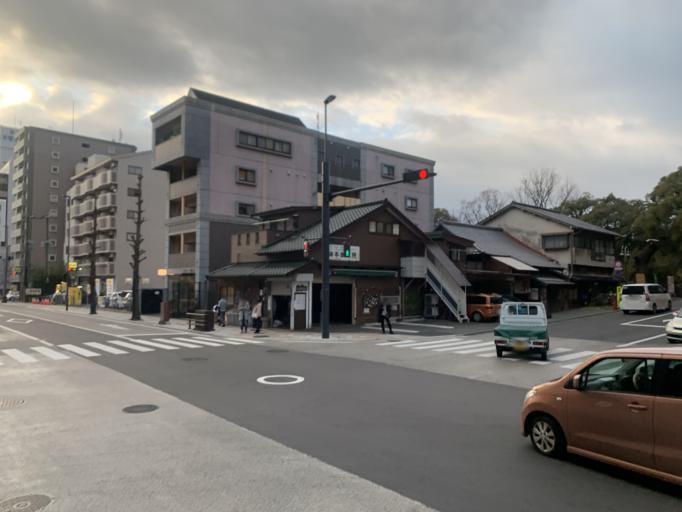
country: JP
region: Kumamoto
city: Kumamoto
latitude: 32.8014
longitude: 130.7029
